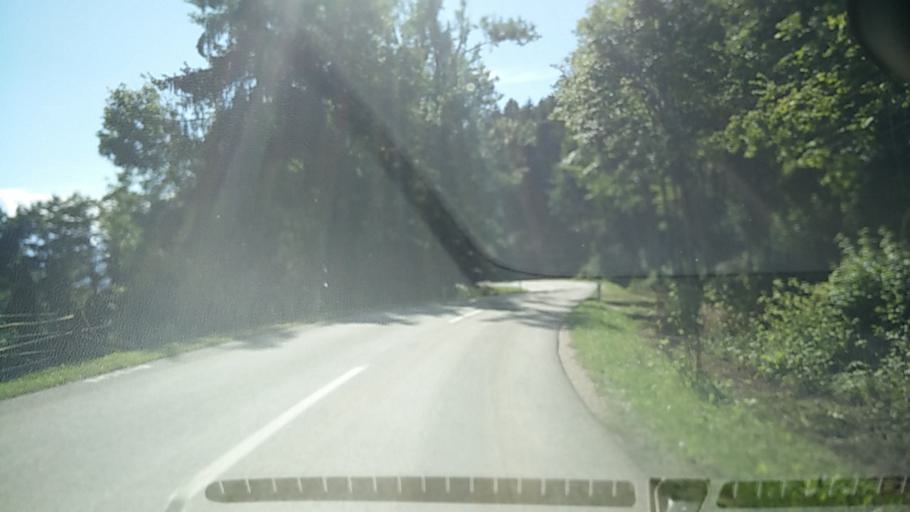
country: AT
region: Carinthia
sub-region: Politischer Bezirk Klagenfurt Land
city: Maria Saal
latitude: 46.7100
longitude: 14.4118
